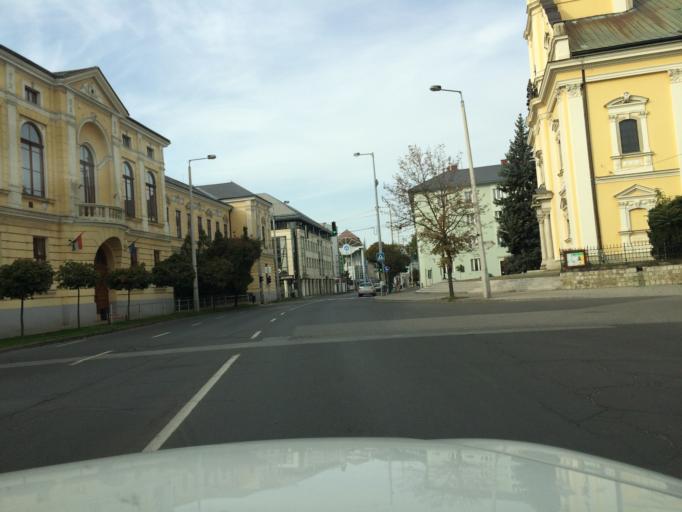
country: HU
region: Szabolcs-Szatmar-Bereg
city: Nyiregyhaza
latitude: 47.9525
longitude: 21.7184
